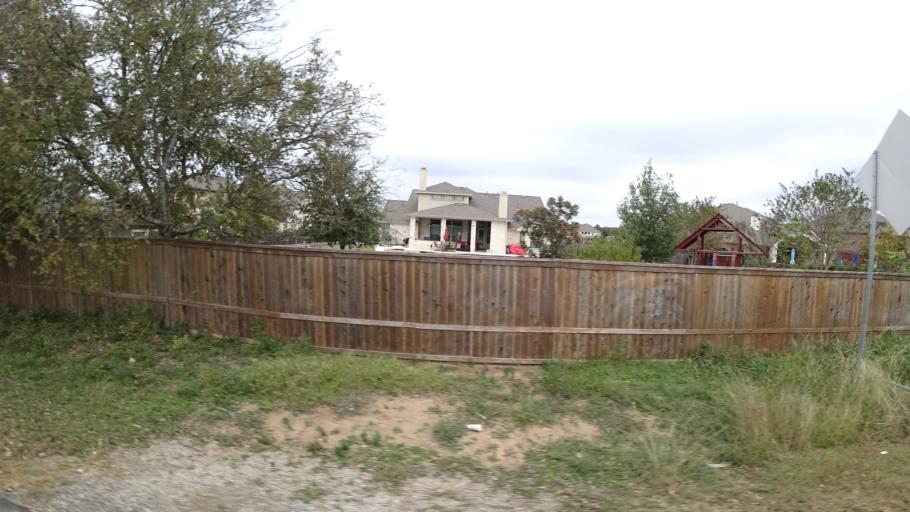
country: US
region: Texas
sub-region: Travis County
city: Shady Hollow
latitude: 30.1479
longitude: -97.8566
